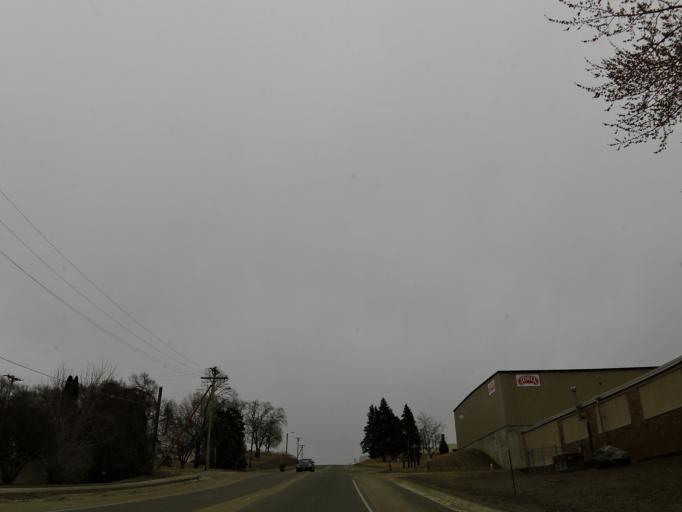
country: US
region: Minnesota
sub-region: Le Sueur County
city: Le Sueur
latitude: 44.4722
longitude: -93.9057
